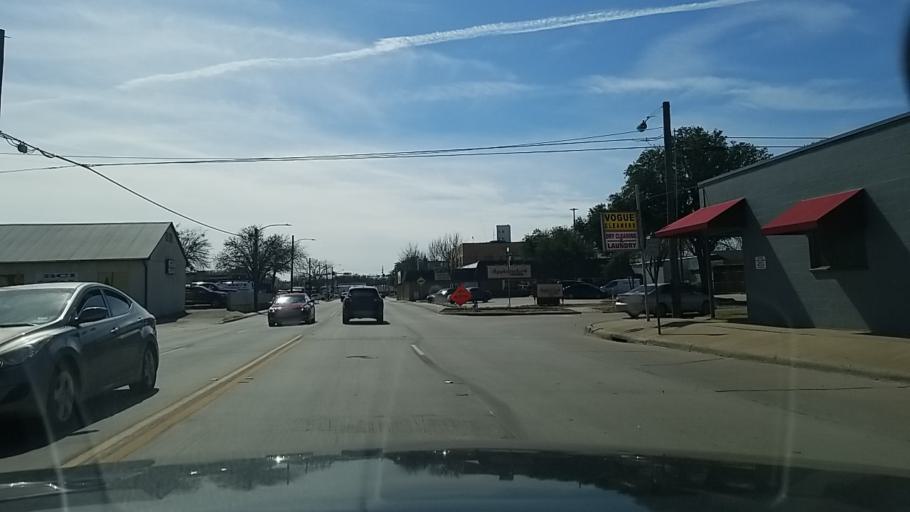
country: US
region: Texas
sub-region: Denton County
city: Denton
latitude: 33.2158
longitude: -97.1283
